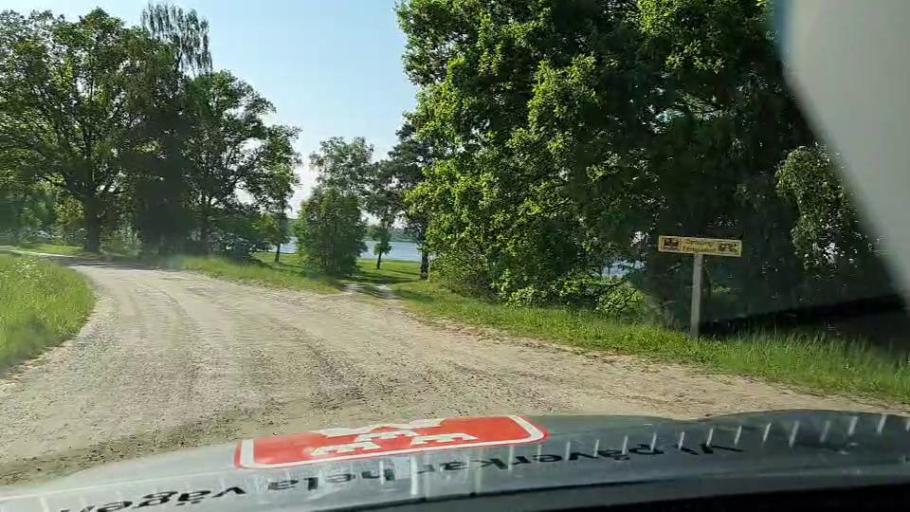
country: SE
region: Skane
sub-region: Hassleholms Kommun
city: Tormestorp
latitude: 56.1167
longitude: 13.7174
